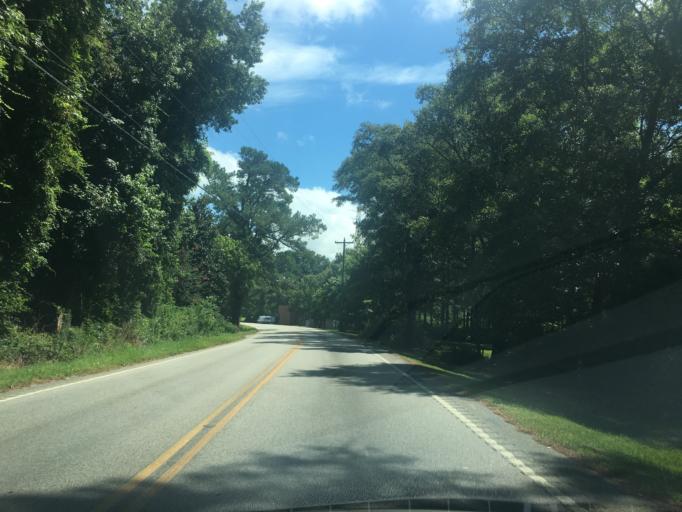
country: US
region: South Carolina
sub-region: Horry County
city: North Myrtle Beach
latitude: 33.8623
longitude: -78.7274
